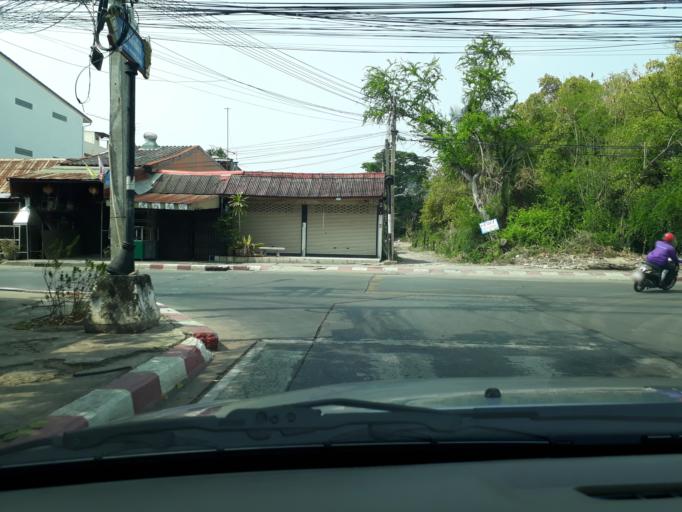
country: TH
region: Khon Kaen
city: Khon Kaen
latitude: 16.4241
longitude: 102.8365
